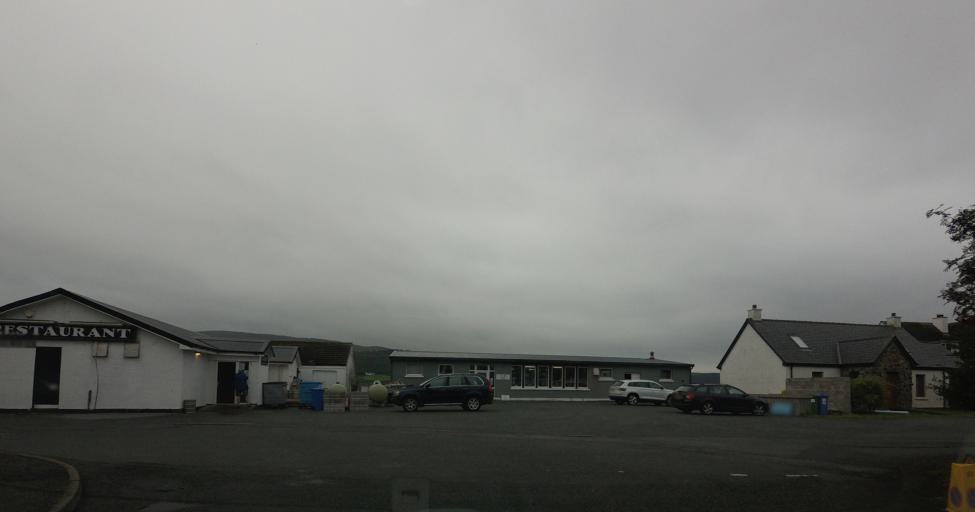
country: GB
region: Scotland
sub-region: Highland
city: Portree
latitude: 57.5863
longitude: -6.3772
